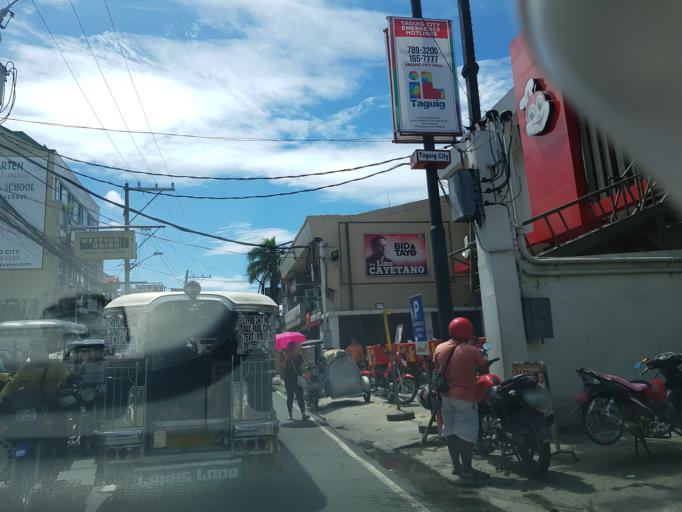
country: PH
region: Calabarzon
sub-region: Province of Rizal
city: Pateros
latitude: 14.5294
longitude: 121.0704
